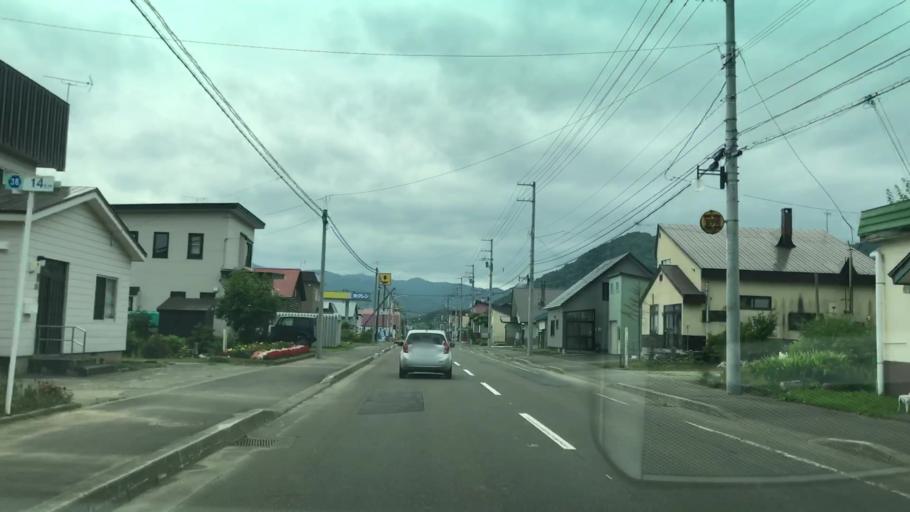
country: JP
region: Hokkaido
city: Yoichi
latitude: 43.0860
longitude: 140.8157
